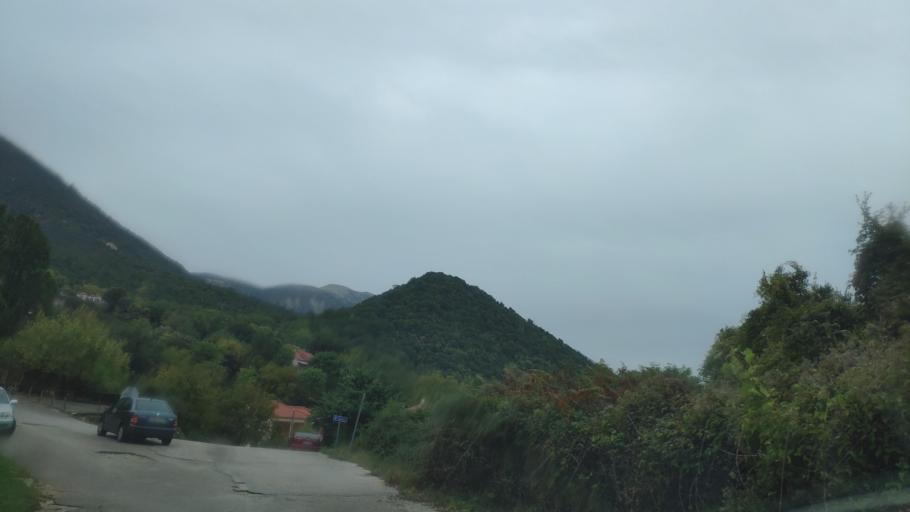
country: GR
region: Epirus
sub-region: Nomos Thesprotias
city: Paramythia
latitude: 39.4171
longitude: 20.6231
